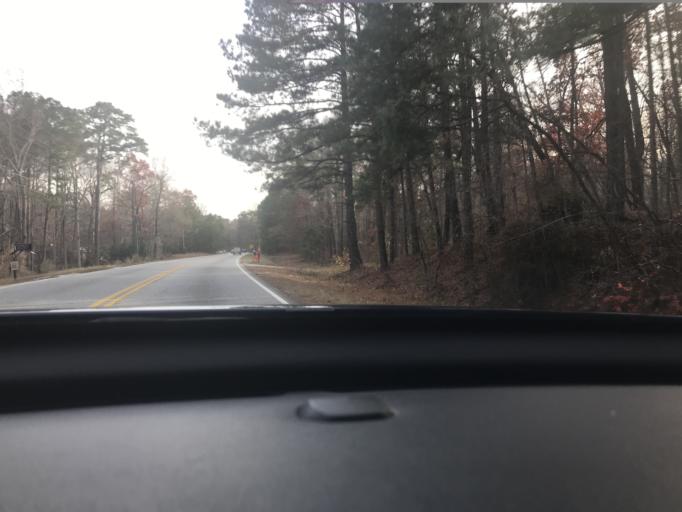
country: US
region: Georgia
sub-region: Newton County
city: Porterdale
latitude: 33.5906
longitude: -83.9131
